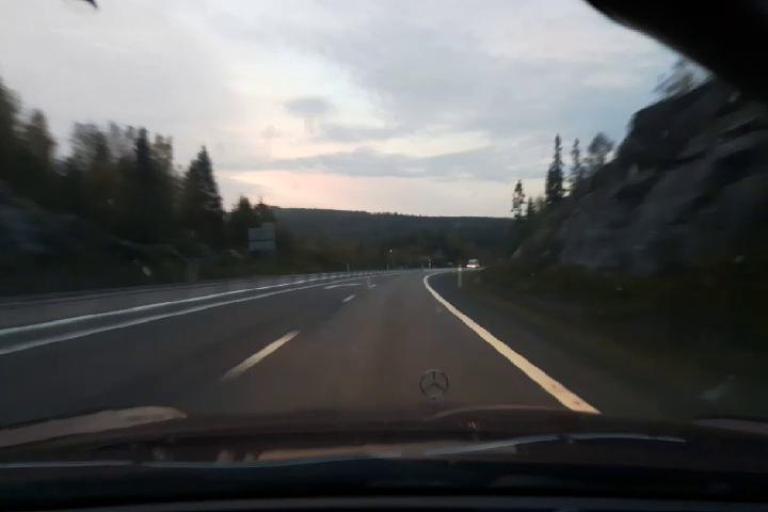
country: SE
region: Vaesternorrland
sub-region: Kramfors Kommun
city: Nordingra
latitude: 62.9505
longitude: 18.0949
